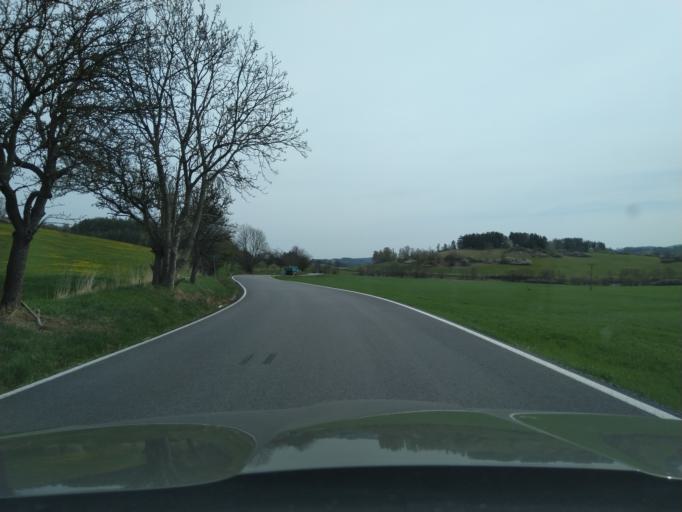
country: CZ
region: Jihocesky
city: Ckyne
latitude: 49.1148
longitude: 13.7799
